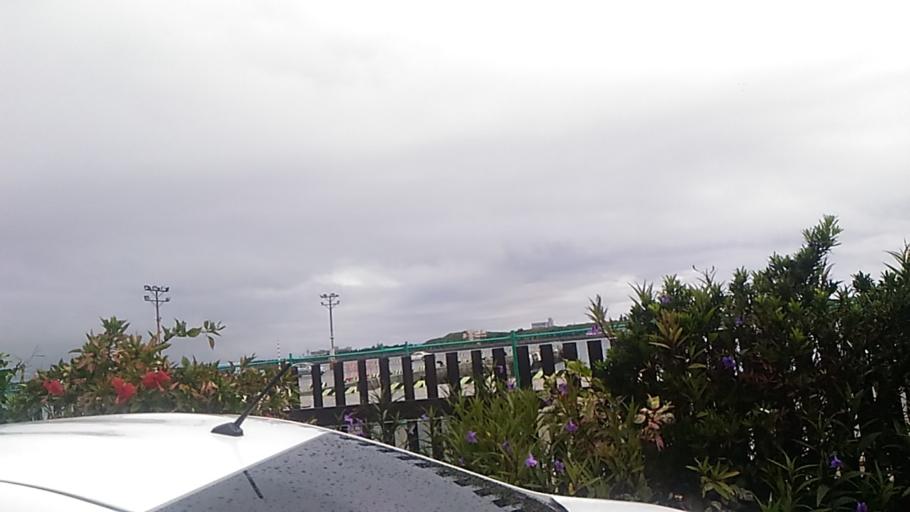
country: TW
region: Taiwan
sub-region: Penghu
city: Ma-kung
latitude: 23.5628
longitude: 119.5654
